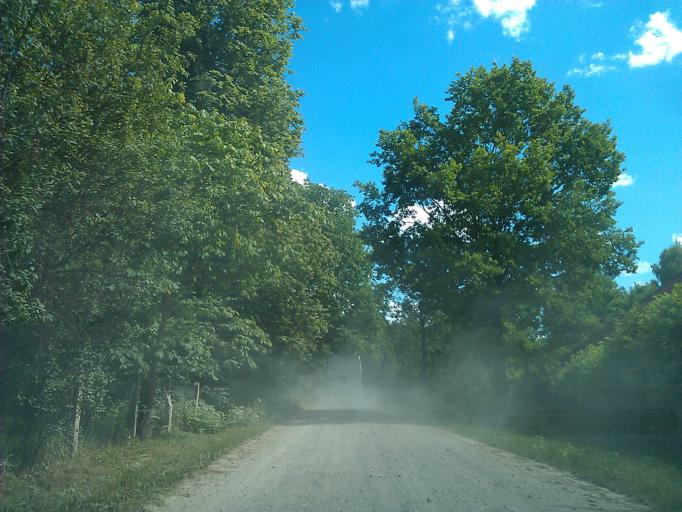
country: LV
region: Vilanu
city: Vilani
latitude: 56.5901
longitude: 26.9503
